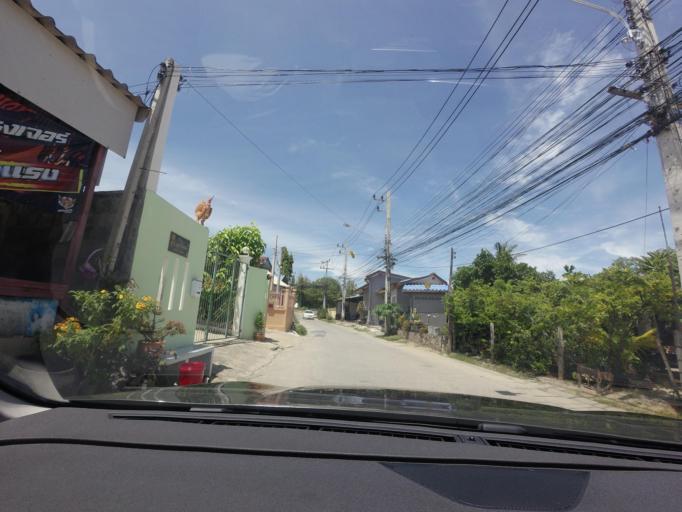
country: TH
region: Prachuap Khiri Khan
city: Hua Hin
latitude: 12.5152
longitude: 99.9727
